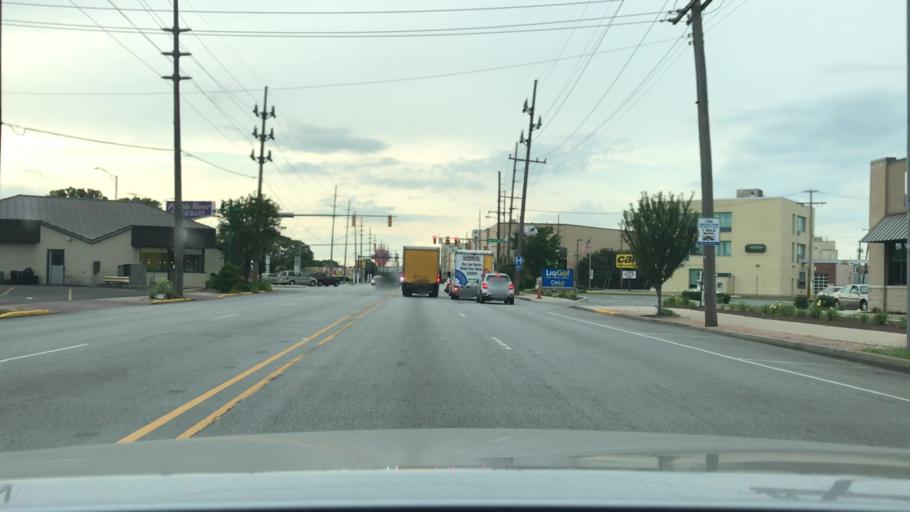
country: US
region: Indiana
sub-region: Lake County
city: Whiting
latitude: 41.6871
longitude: -87.5075
